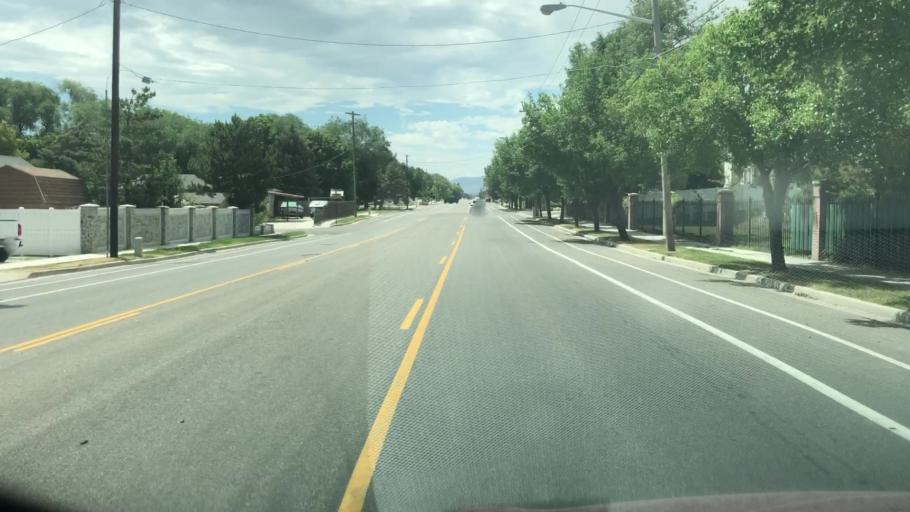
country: US
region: Utah
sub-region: Salt Lake County
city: South Jordan
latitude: 40.5529
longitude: -111.9292
